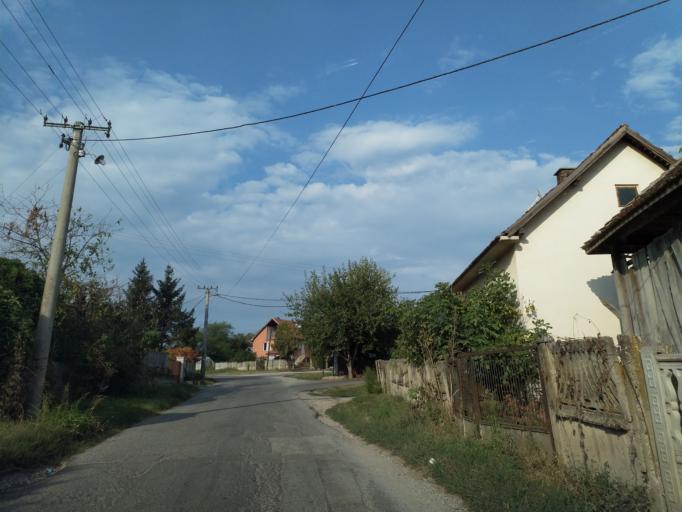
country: RS
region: Central Serbia
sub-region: Pomoravski Okrug
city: Paracin
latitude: 43.8417
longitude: 21.4791
